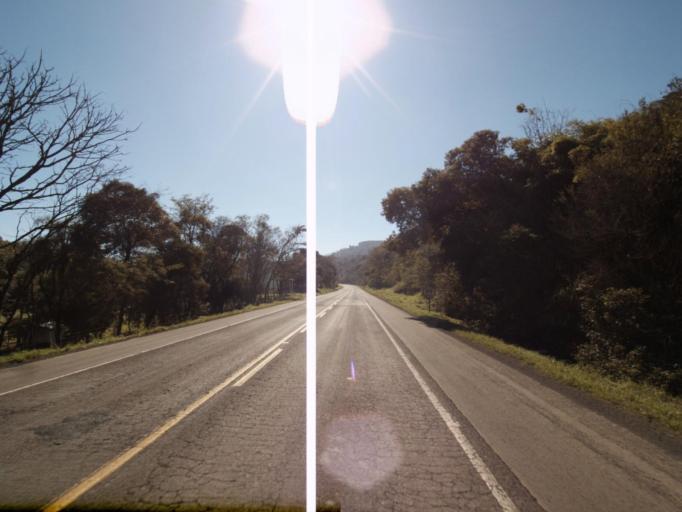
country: BR
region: Rio Grande do Sul
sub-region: Frederico Westphalen
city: Frederico Westphalen
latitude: -27.0152
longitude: -53.2271
